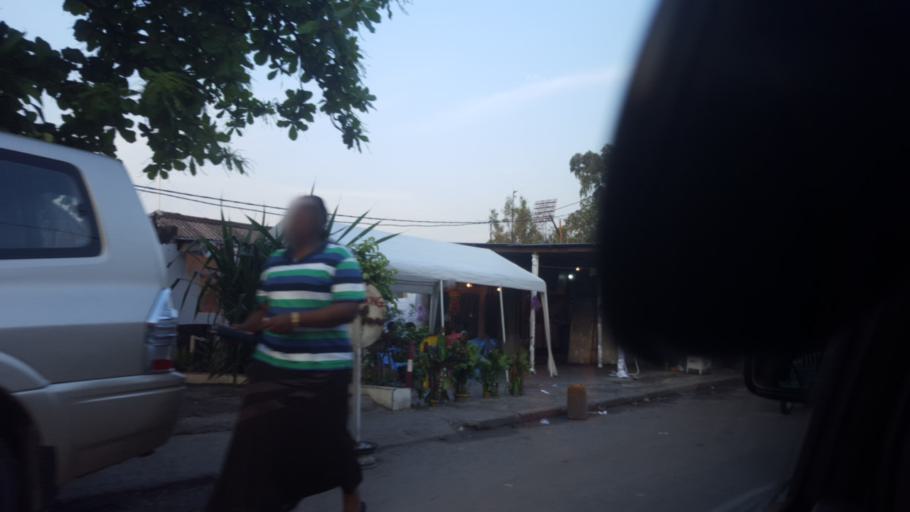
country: CD
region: Kinshasa
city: Kinshasa
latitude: -4.3378
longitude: 15.3192
